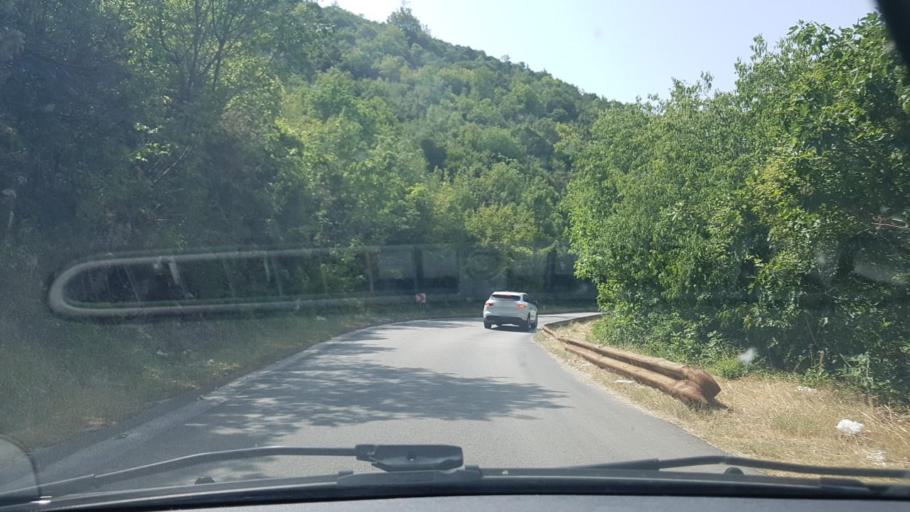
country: BA
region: Federation of Bosnia and Herzegovina
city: Tasovcici
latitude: 43.0285
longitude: 17.7464
